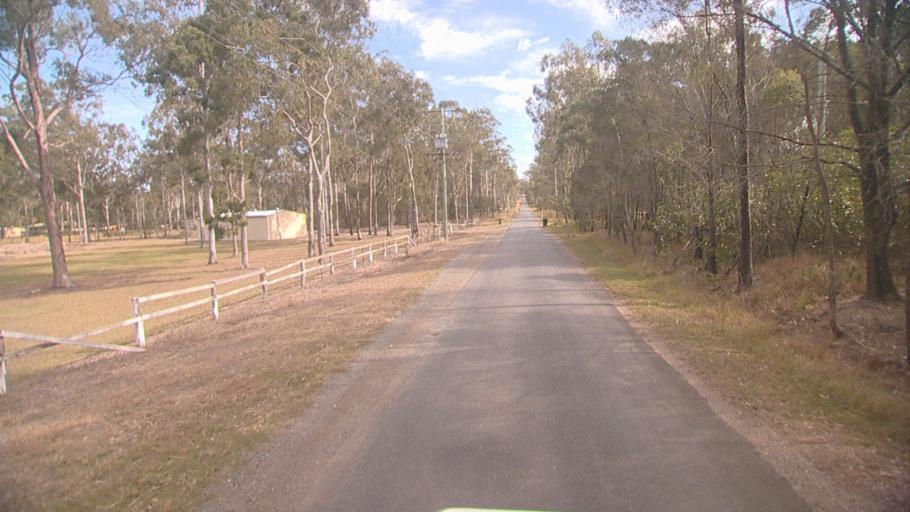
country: AU
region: Queensland
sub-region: Logan
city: North Maclean
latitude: -27.7482
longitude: 152.9810
